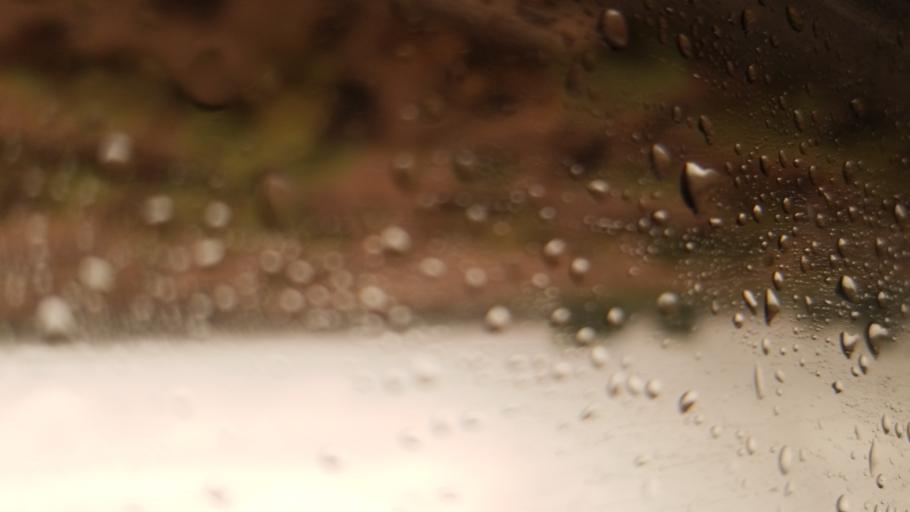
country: US
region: Arizona
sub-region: Navajo County
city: Joseph City
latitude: 34.9187
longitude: -110.2722
